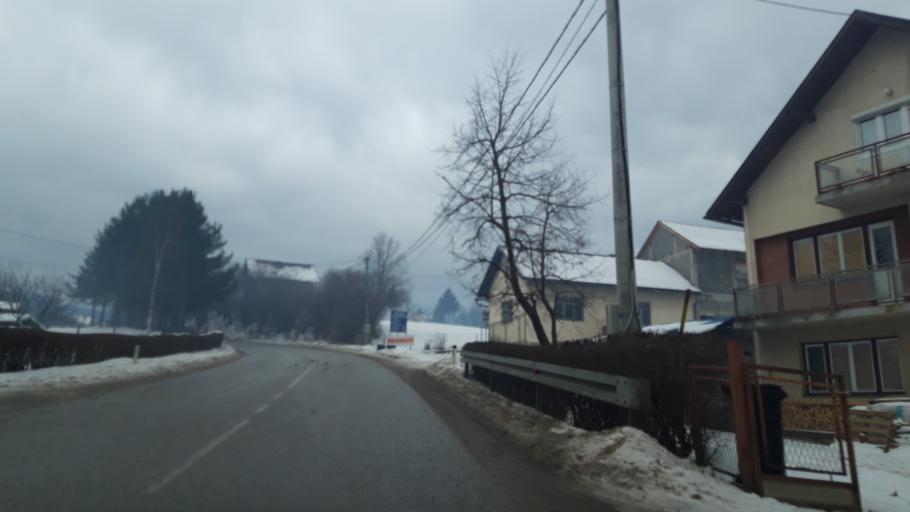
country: BA
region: Republika Srpska
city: Koran
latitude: 43.8115
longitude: 18.5577
